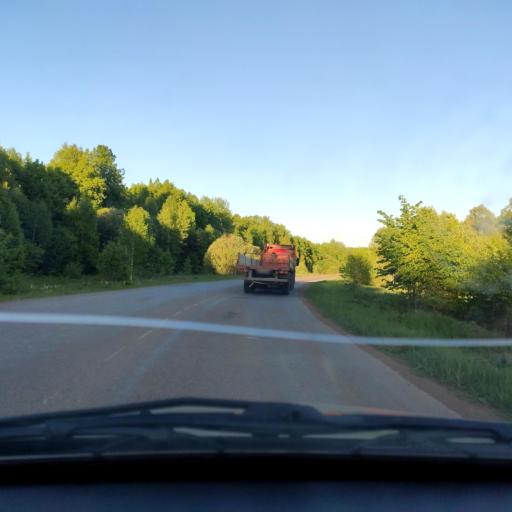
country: RU
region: Bashkortostan
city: Blagoveshchensk
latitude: 55.0319
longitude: 56.1026
